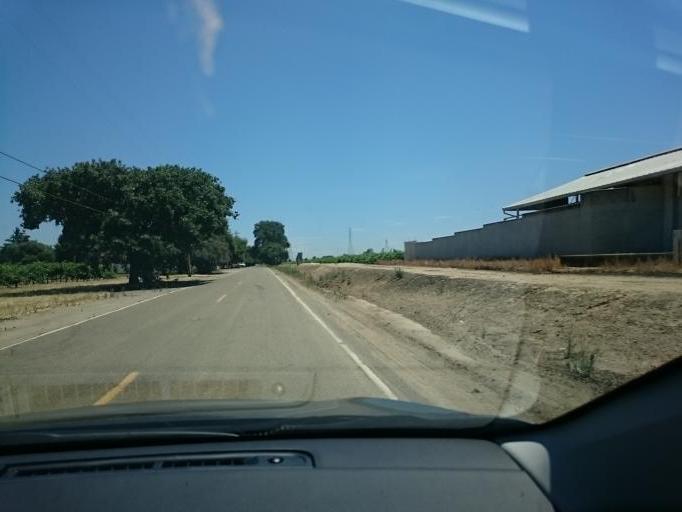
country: US
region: California
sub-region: San Joaquin County
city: Thornton
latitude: 38.2039
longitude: -121.3871
